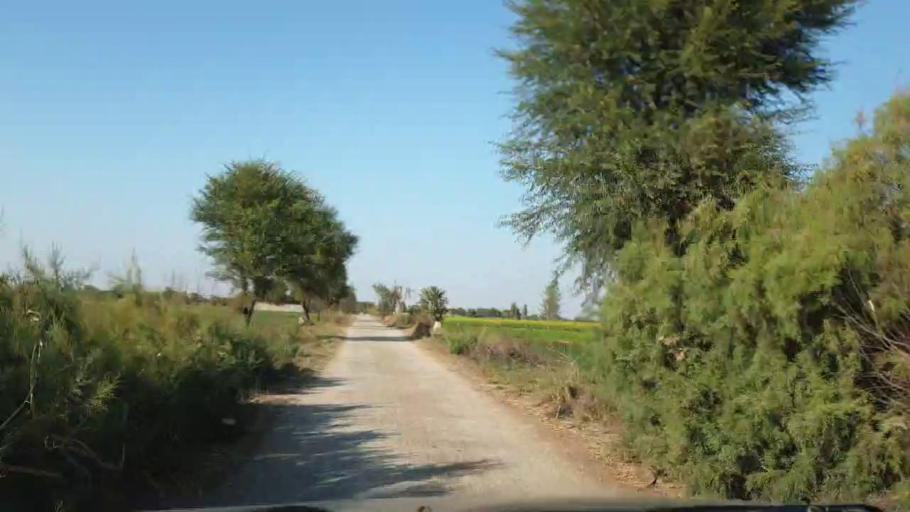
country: PK
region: Sindh
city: Khadro
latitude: 26.2098
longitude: 68.7543
